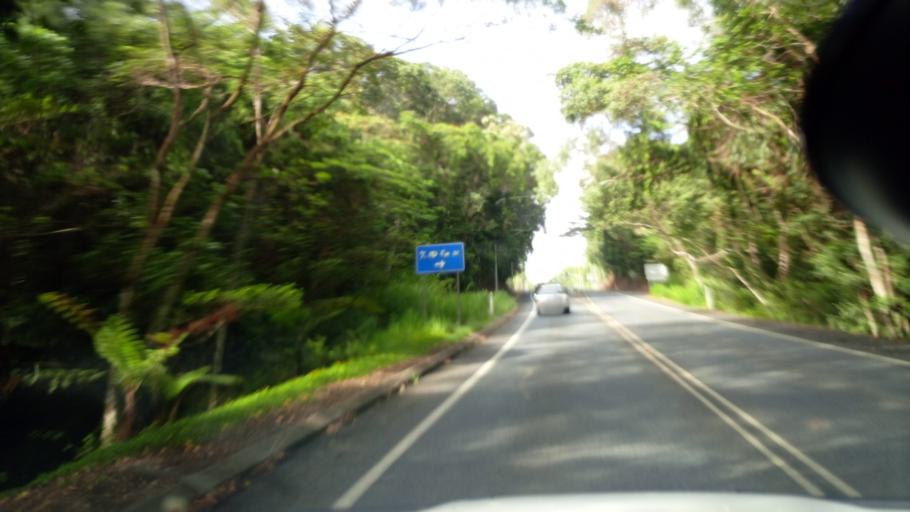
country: AU
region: Queensland
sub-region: Tablelands
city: Kuranda
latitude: -16.8219
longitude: 145.6271
